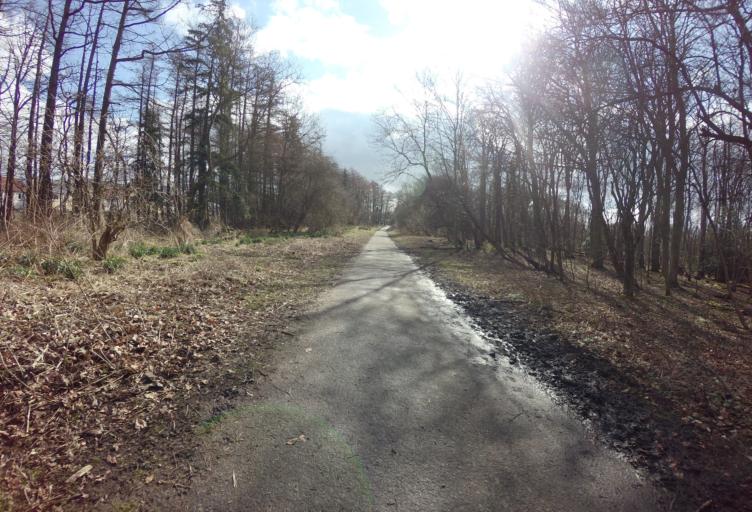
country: GB
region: Scotland
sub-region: West Lothian
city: East Calder
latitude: 55.8990
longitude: -3.4577
